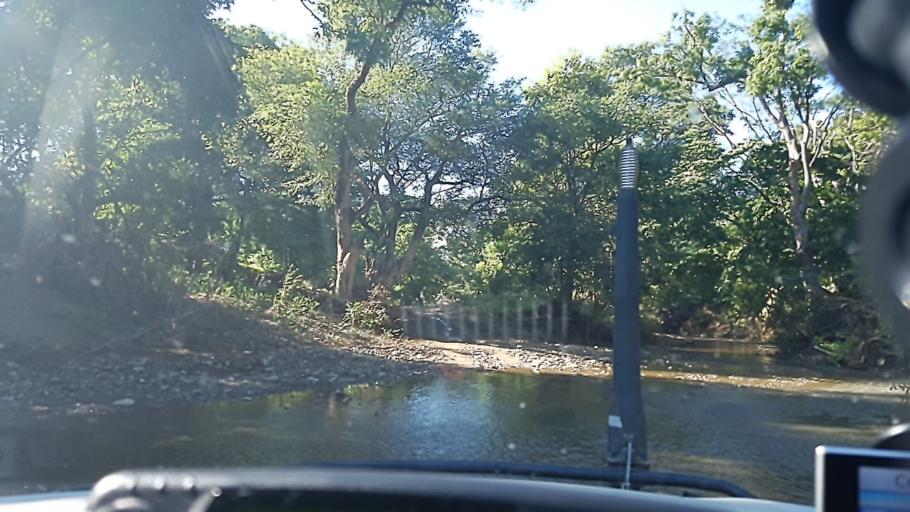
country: NI
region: Rivas
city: Tola
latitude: 11.5401
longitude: -86.1234
